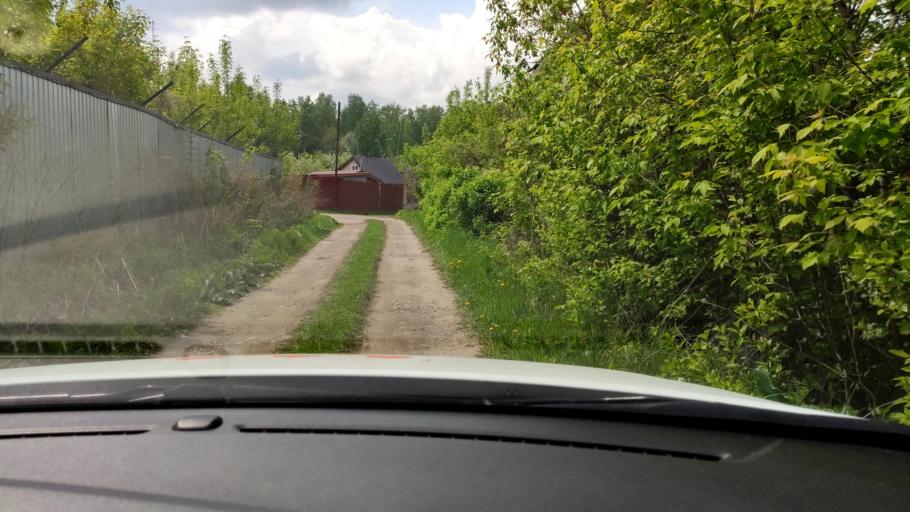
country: RU
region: Tatarstan
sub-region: Gorod Kazan'
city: Kazan
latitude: 55.8248
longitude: 49.1781
